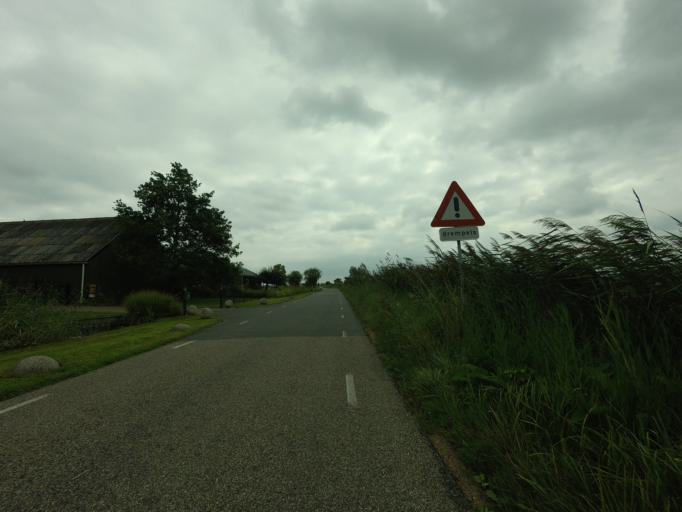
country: NL
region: Utrecht
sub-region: Stichtse Vecht
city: Breukelen
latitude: 52.1999
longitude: 4.9361
